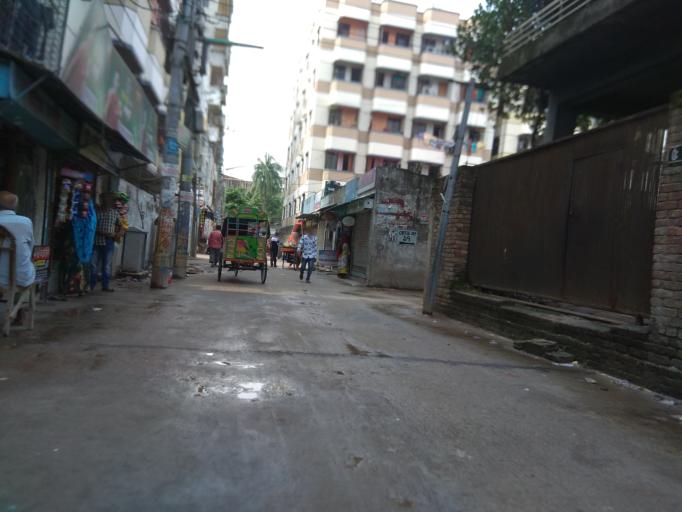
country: BD
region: Dhaka
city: Azimpur
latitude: 23.7985
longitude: 90.3583
